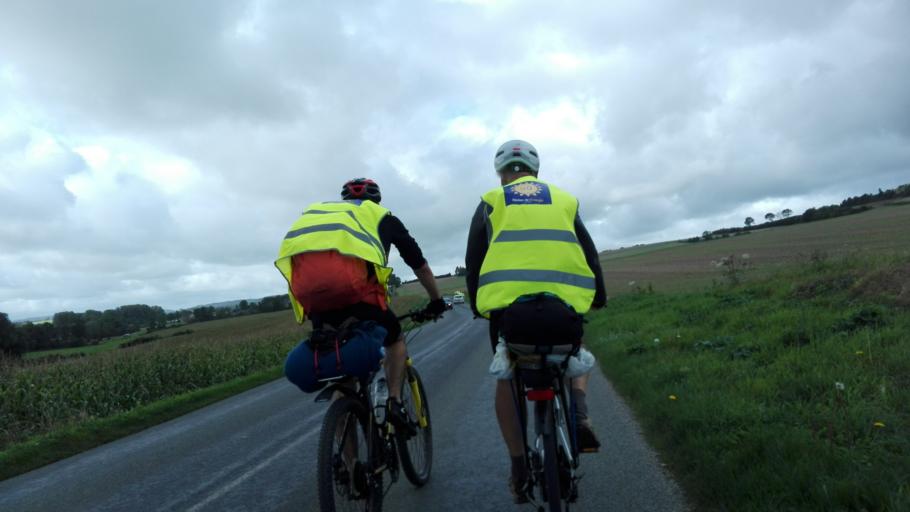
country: FR
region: Nord-Pas-de-Calais
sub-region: Departement du Pas-de-Calais
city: Licques
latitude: 50.7905
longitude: 1.9837
